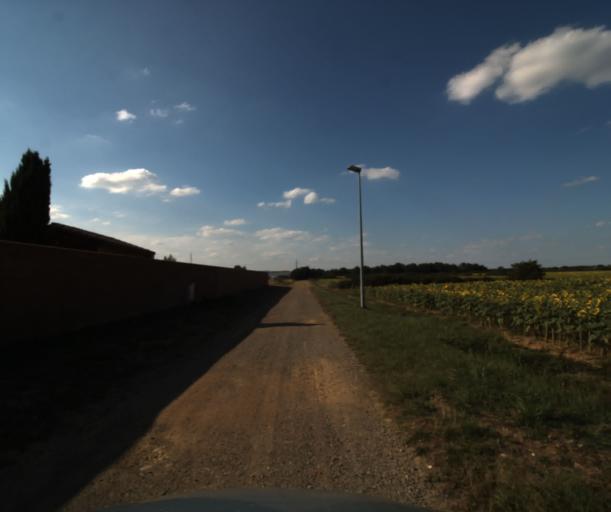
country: FR
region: Midi-Pyrenees
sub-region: Departement de la Haute-Garonne
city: Saint-Lys
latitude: 43.5082
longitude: 1.2005
